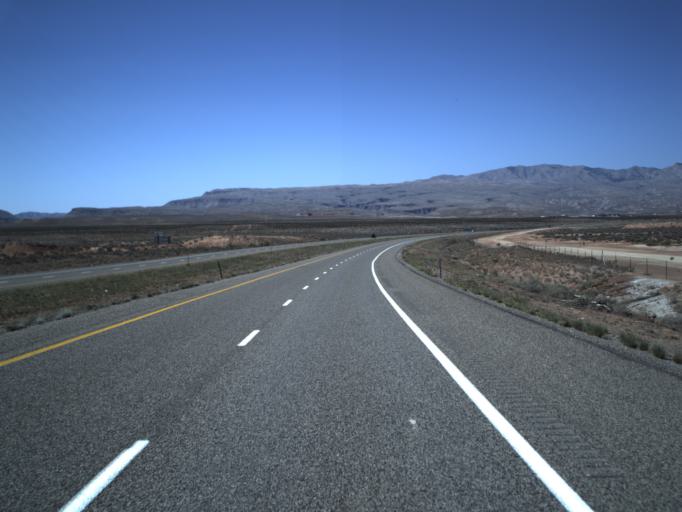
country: US
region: Utah
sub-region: Washington County
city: Saint George
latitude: 37.0008
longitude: -113.5705
